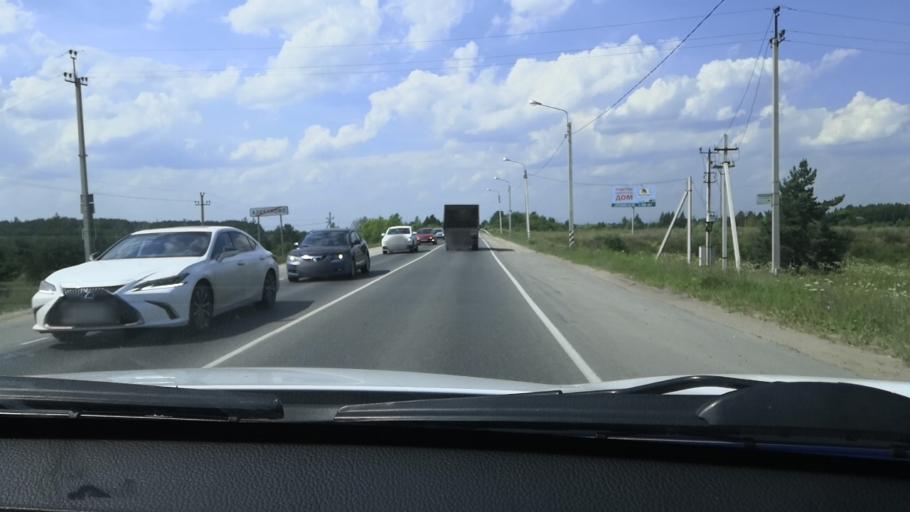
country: RU
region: Rjazan
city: Murmino
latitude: 54.6322
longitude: 39.9510
